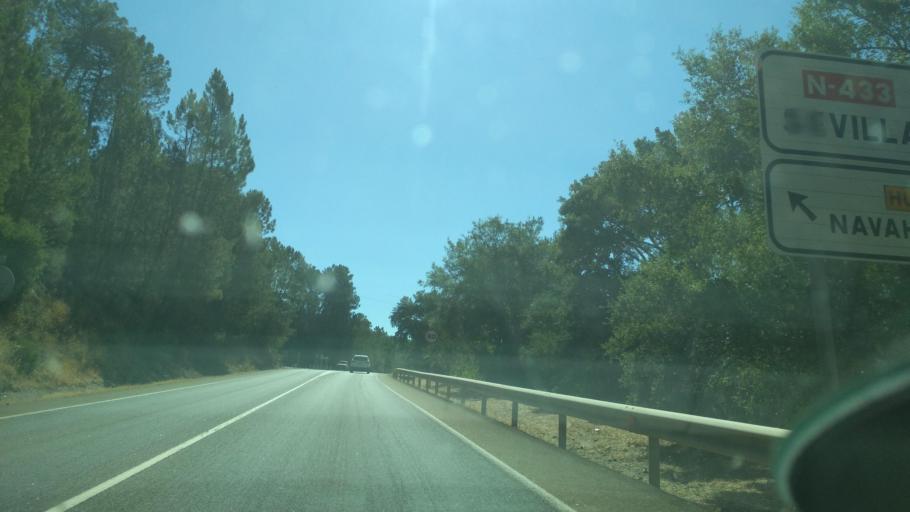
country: ES
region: Andalusia
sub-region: Provincia de Huelva
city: Fuenteheridos
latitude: 37.9165
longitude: -6.6686
